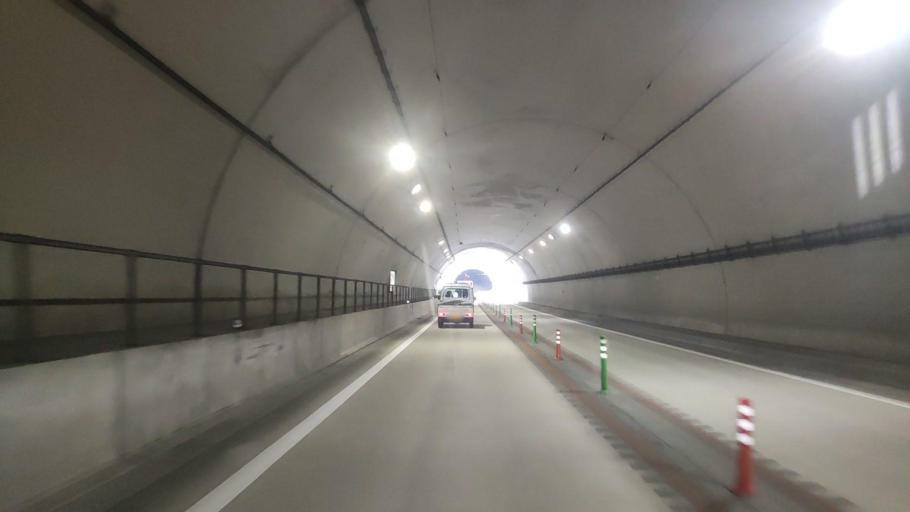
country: JP
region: Wakayama
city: Tanabe
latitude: 33.6117
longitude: 135.4254
